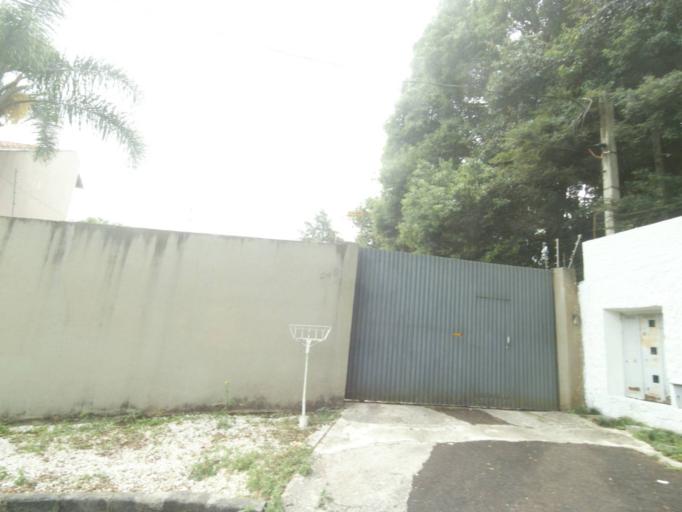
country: BR
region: Parana
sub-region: Curitiba
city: Curitiba
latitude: -25.4350
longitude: -49.3214
